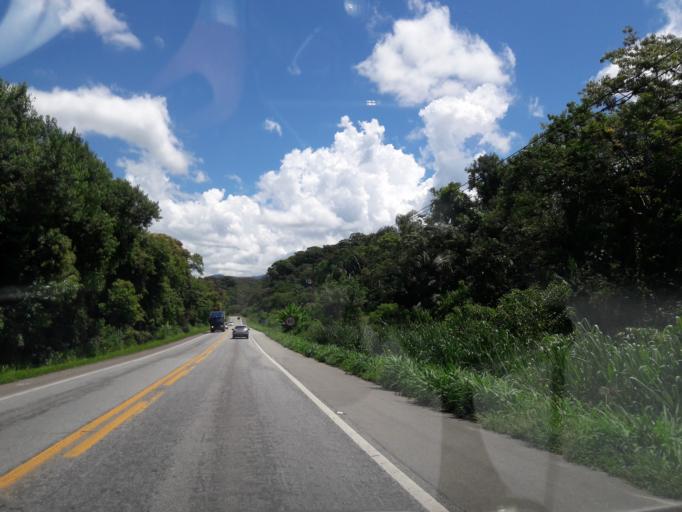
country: BR
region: Parana
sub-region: Antonina
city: Antonina
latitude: -25.4491
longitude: -48.8011
